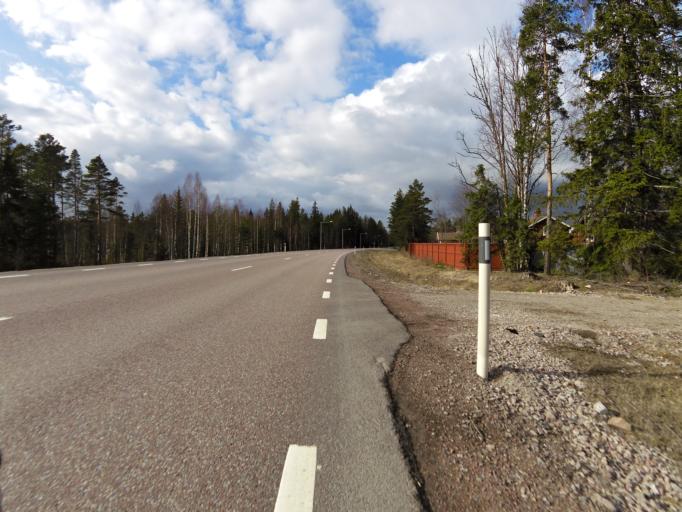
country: SE
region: Gaevleborg
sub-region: Hofors Kommun
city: Hofors
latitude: 60.4945
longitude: 16.4354
